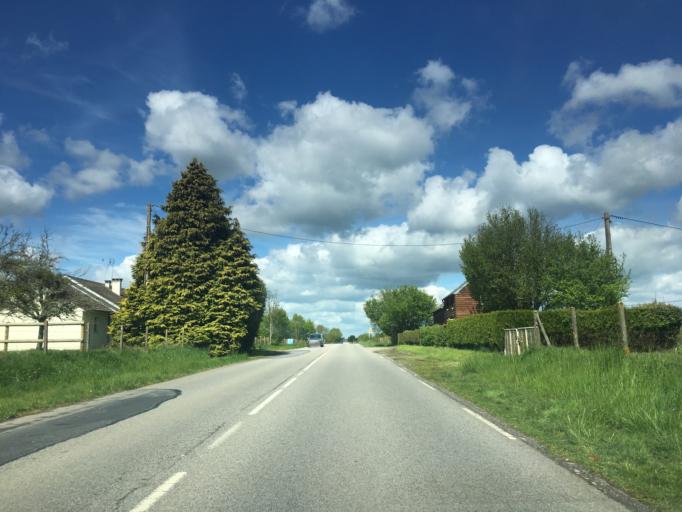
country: FR
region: Lower Normandy
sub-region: Departement de l'Orne
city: Rai
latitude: 48.8295
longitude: 0.5523
